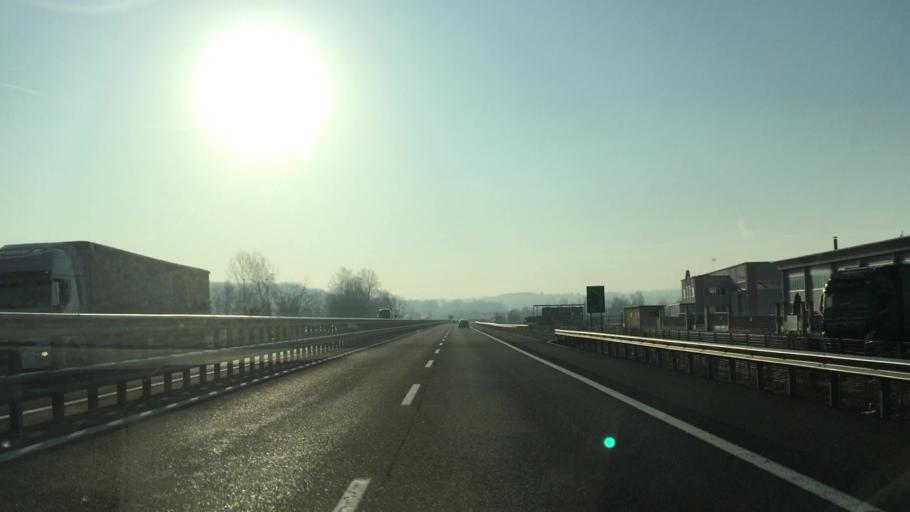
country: IT
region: Piedmont
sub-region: Provincia di Asti
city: Villafranca d'Asti
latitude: 44.9136
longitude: 8.0402
